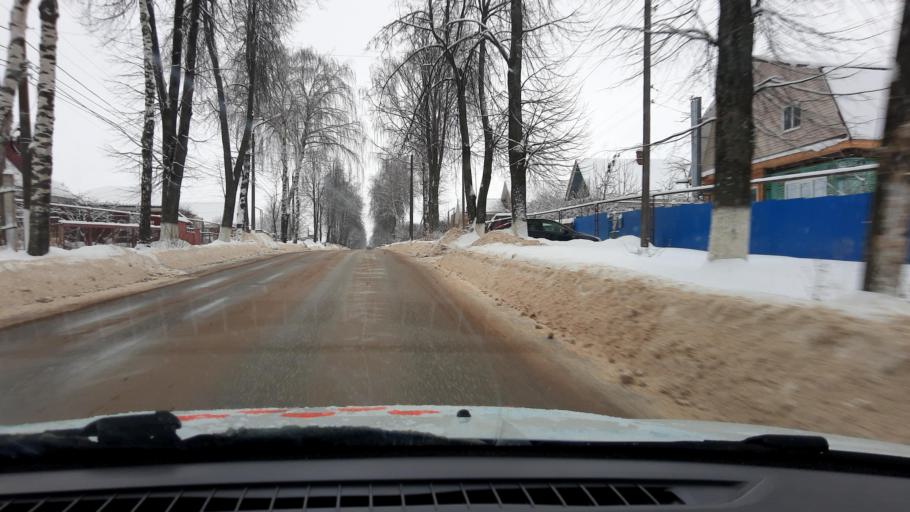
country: RU
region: Nizjnij Novgorod
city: Chkalovsk
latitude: 56.7622
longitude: 43.2420
